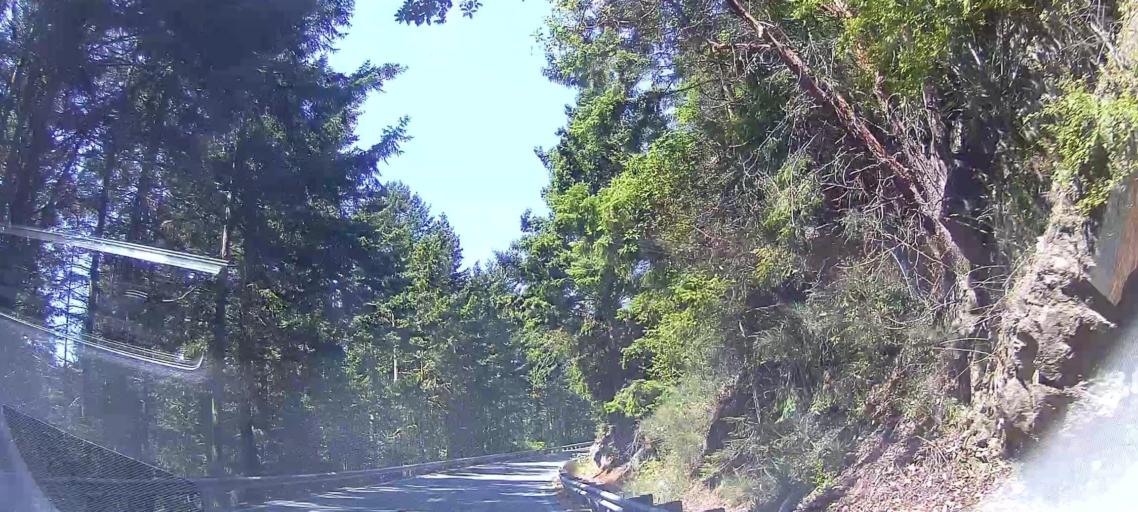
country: US
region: Washington
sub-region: Island County
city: Ault Field
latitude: 48.4218
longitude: -122.6611
